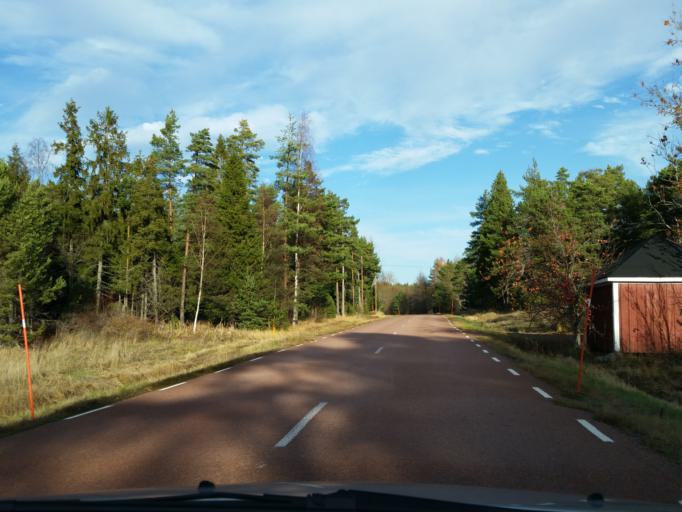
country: AX
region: Alands landsbygd
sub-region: Saltvik
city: Saltvik
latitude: 60.3580
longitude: 20.1008
